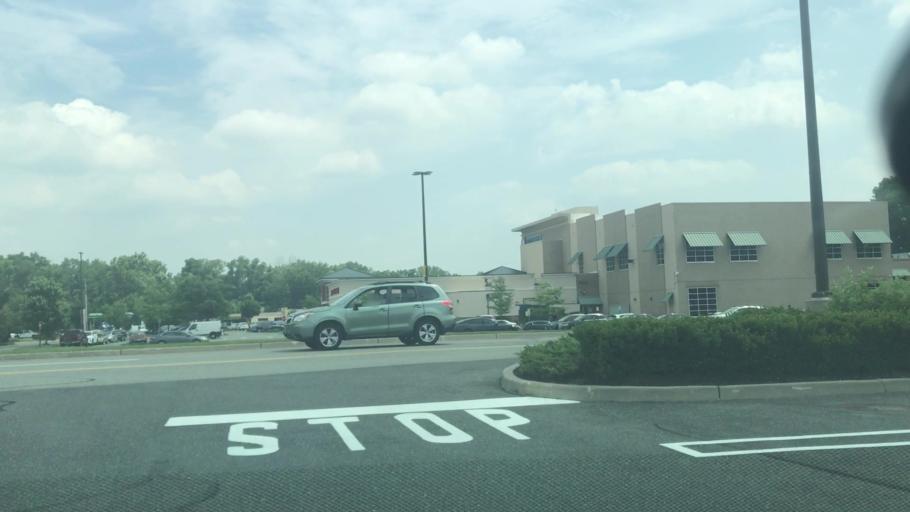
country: US
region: New Jersey
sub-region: Bergen County
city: Maywood
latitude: 40.9131
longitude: -74.0514
